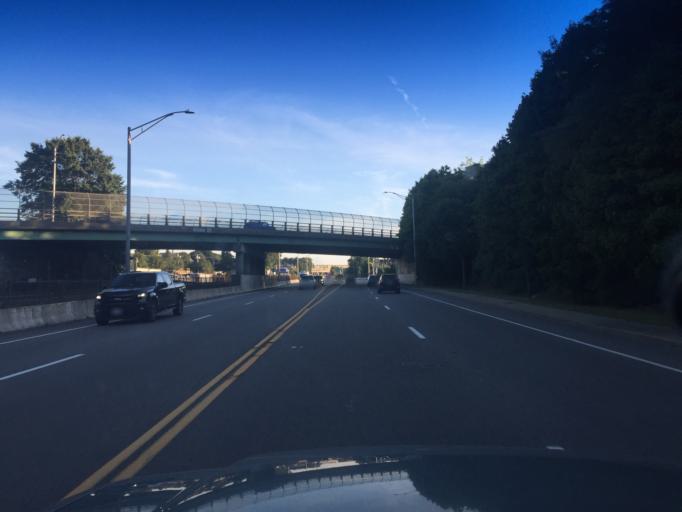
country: US
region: Massachusetts
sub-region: Norfolk County
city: Quincy
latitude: 42.2421
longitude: -71.0050
